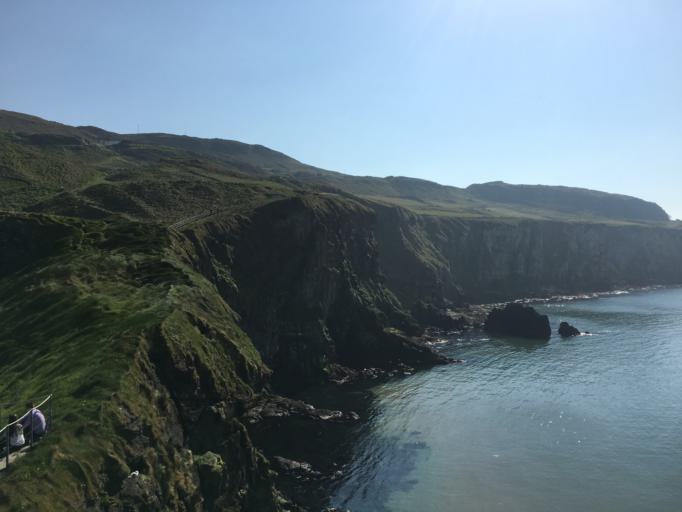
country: GB
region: Northern Ireland
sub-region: Moyle District
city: Ballycastle
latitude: 55.2402
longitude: -6.3318
